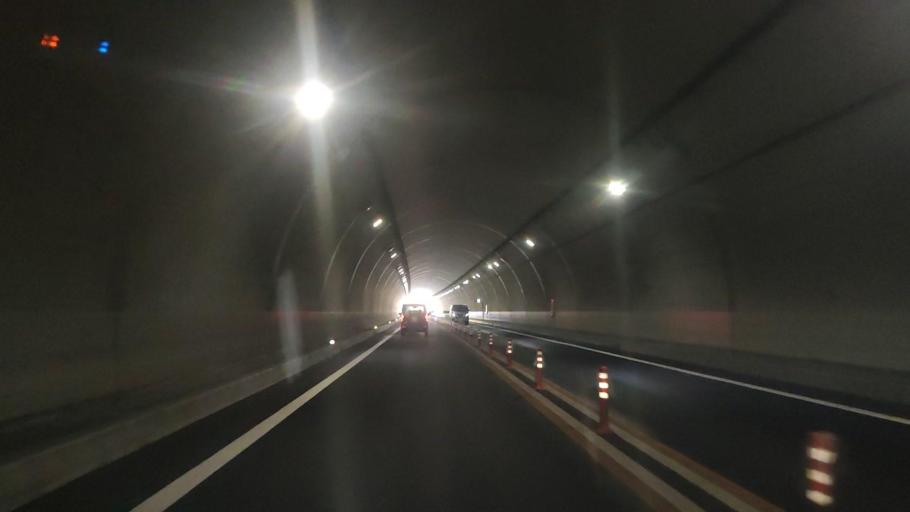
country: JP
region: Fukuoka
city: Nakatsu
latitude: 33.5160
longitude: 131.2743
